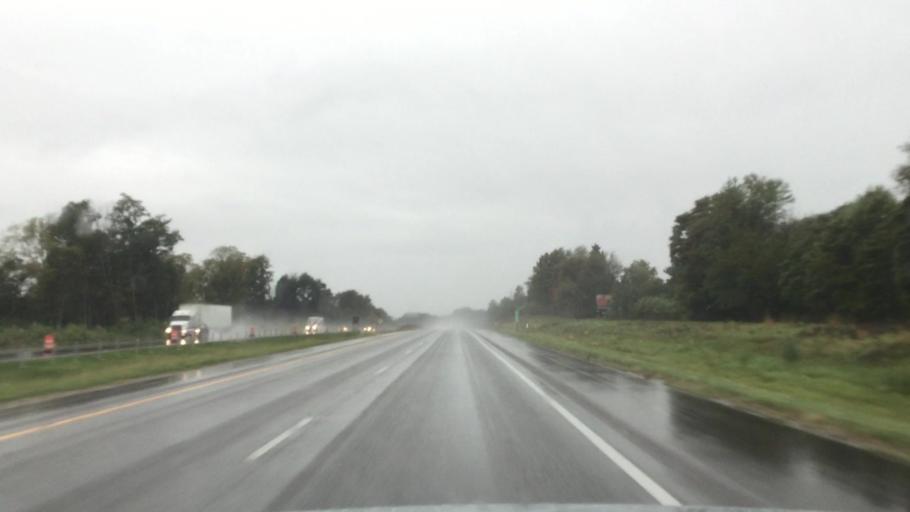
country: US
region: Michigan
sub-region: Van Buren County
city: Hartford
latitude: 42.1975
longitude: -86.0875
